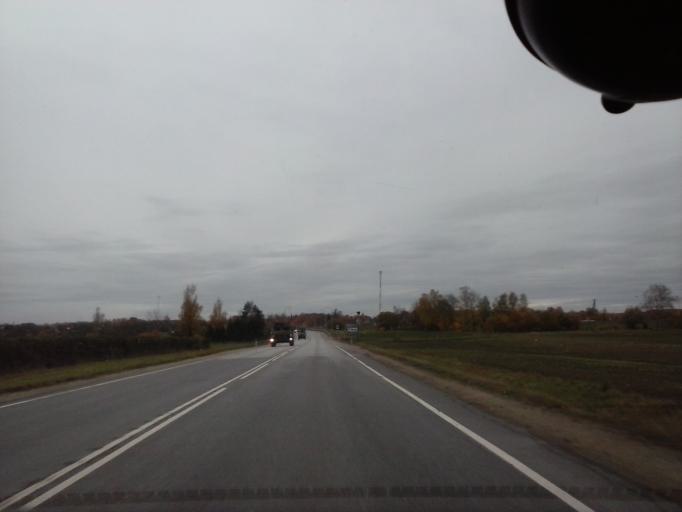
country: EE
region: Jogevamaa
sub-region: Jogeva linn
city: Jogeva
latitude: 58.5614
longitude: 26.2930
